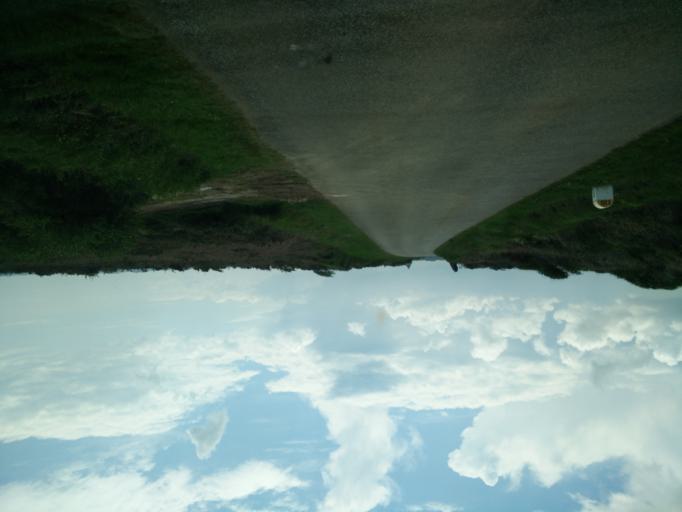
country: FR
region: Brittany
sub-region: Departement du Finistere
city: Roscanvel
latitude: 48.3139
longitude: -4.5713
